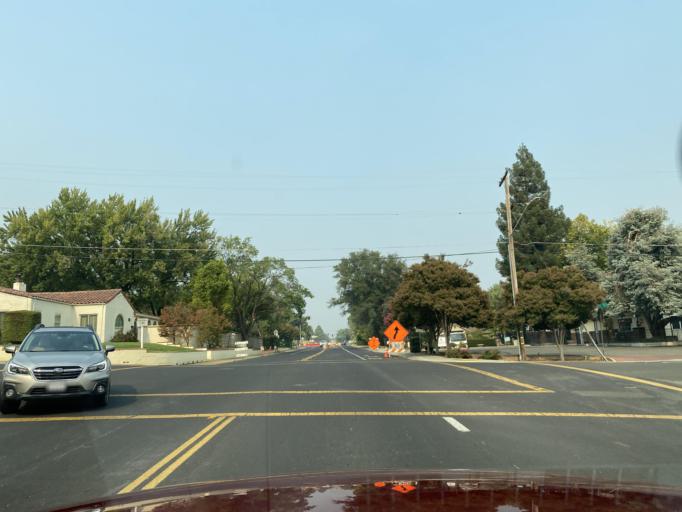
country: US
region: California
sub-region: Sacramento County
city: Folsom
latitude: 38.6759
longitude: -121.1730
